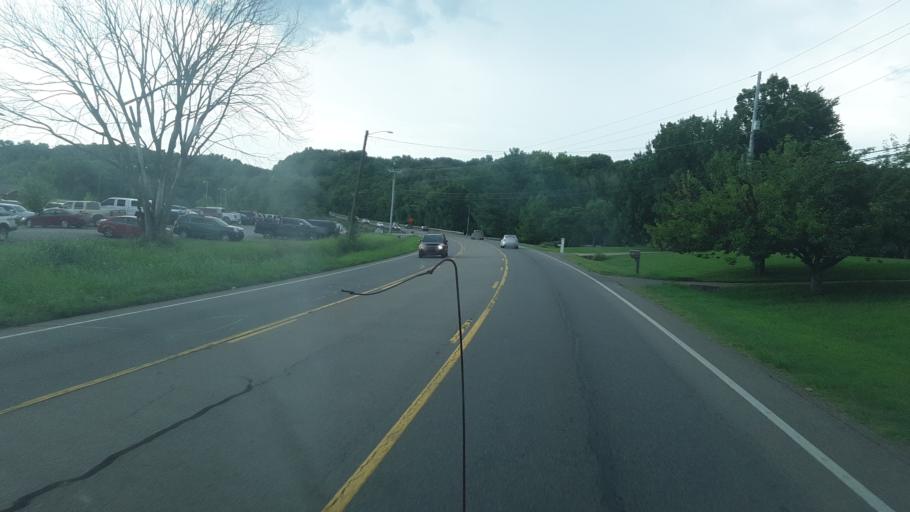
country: US
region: Tennessee
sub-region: Montgomery County
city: Clarksville
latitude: 36.5362
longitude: -87.2835
